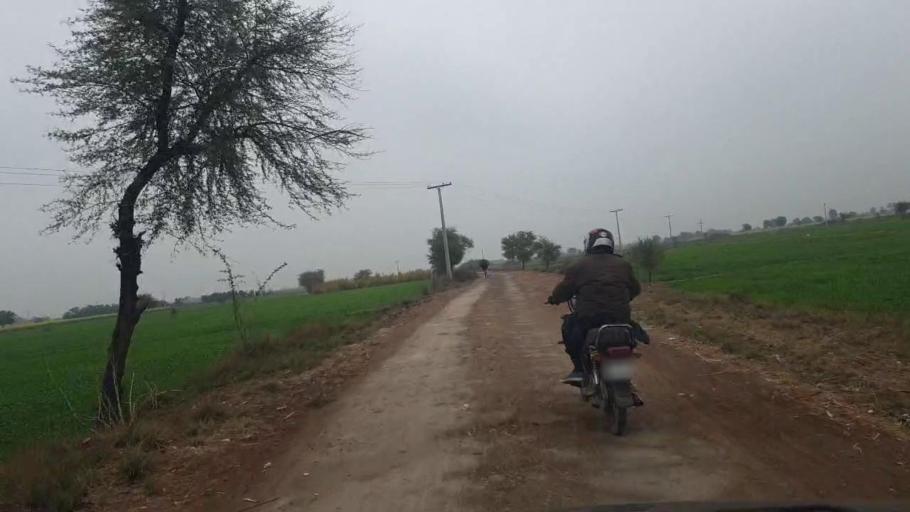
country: PK
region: Sindh
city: Tando Adam
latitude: 25.8433
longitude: 68.7237
